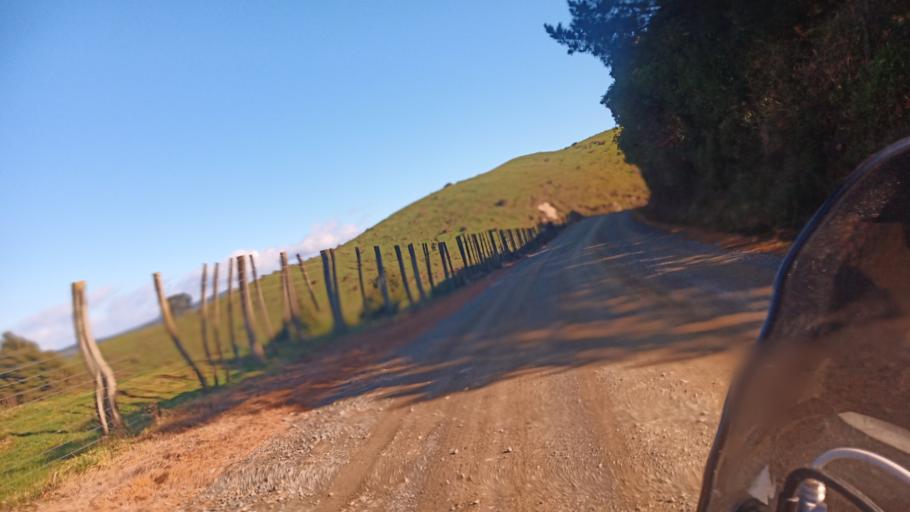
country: NZ
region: Hawke's Bay
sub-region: Wairoa District
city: Wairoa
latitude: -38.7955
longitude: 177.2847
